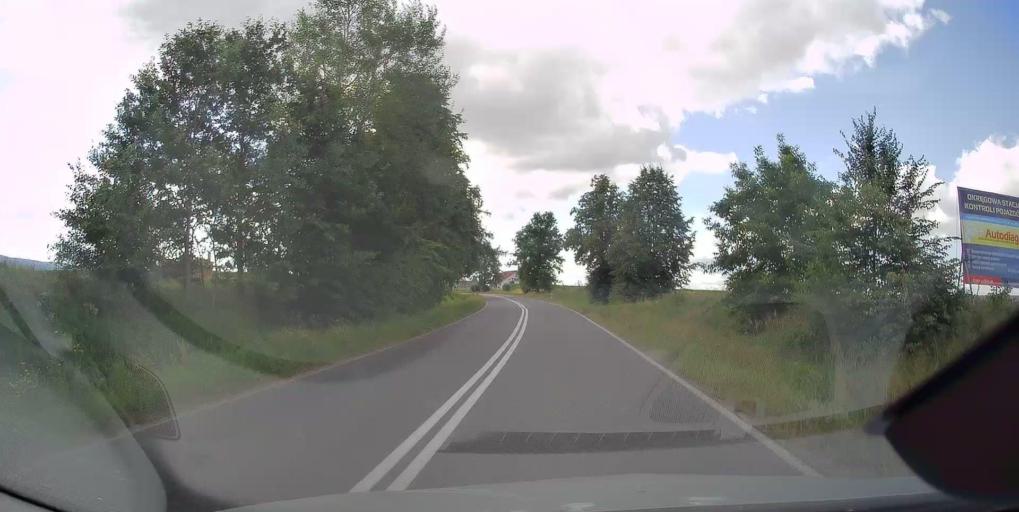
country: PL
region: Swietokrzyskie
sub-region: Powiat kielecki
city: Nowa Slupia
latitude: 50.8917
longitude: 21.0392
